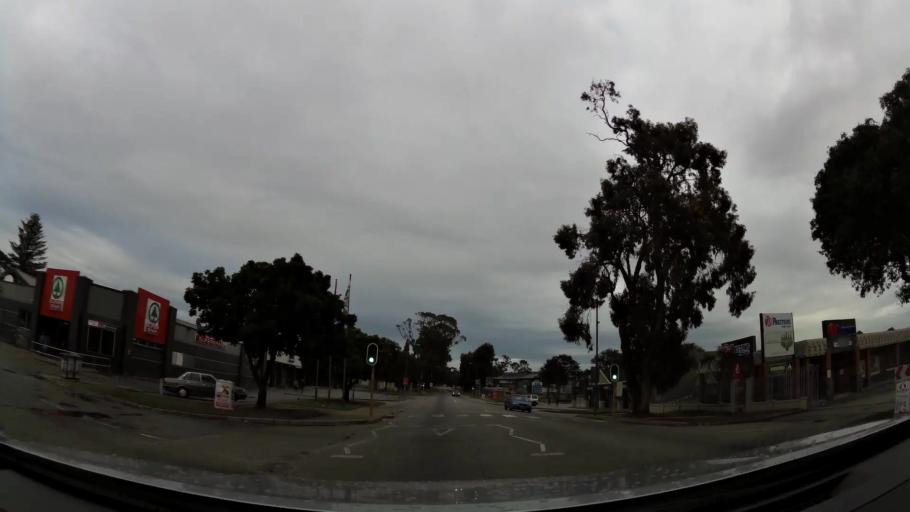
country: ZA
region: Eastern Cape
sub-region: Nelson Mandela Bay Metropolitan Municipality
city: Port Elizabeth
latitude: -33.9788
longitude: 25.5841
